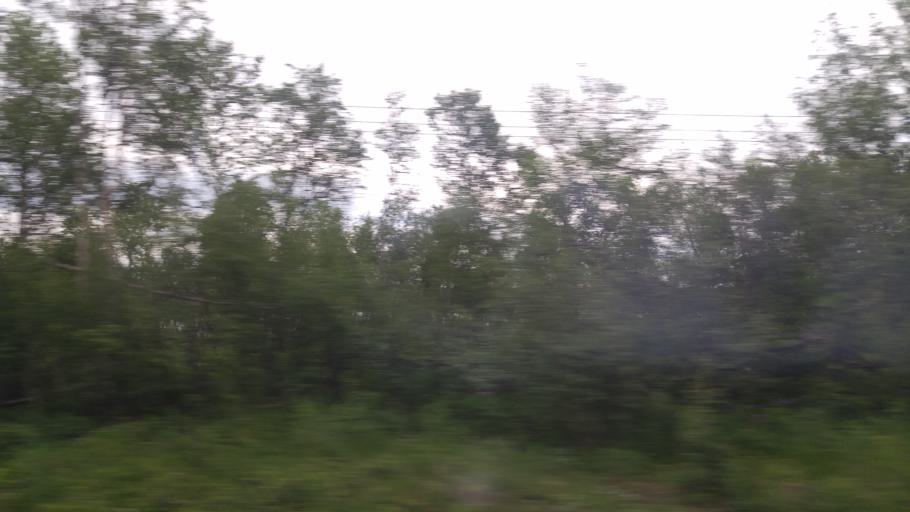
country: NO
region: Nord-Trondelag
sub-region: Meraker
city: Meraker
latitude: 63.3170
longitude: 12.2072
